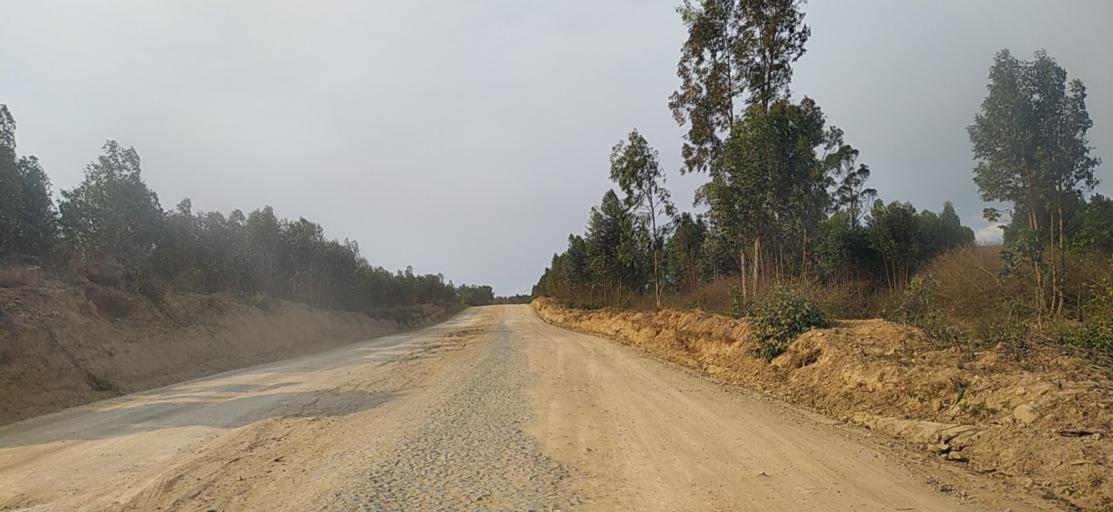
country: MG
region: Alaotra Mangoro
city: Moramanga
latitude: -18.6582
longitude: 48.2741
